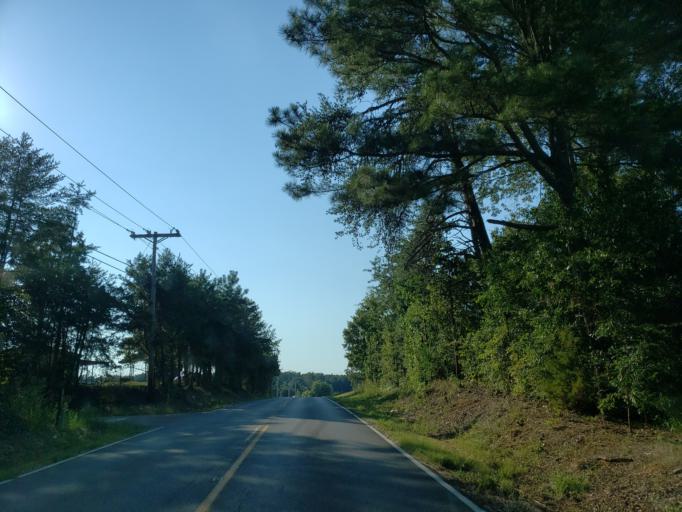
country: US
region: Tennessee
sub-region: Bradley County
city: Wildwood Lake
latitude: 35.0342
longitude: -84.7371
